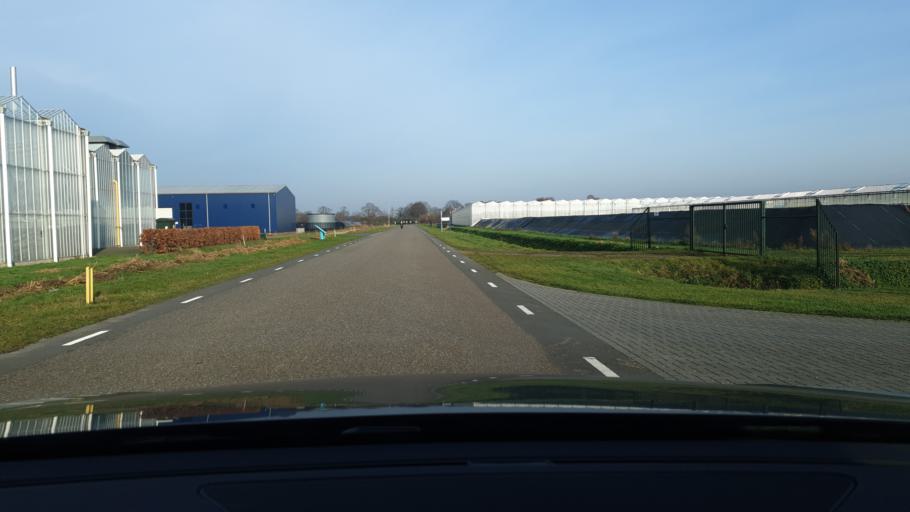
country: NL
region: Limburg
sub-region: Gemeente Peel en Maas
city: Maasbree
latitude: 51.4308
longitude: 6.0820
